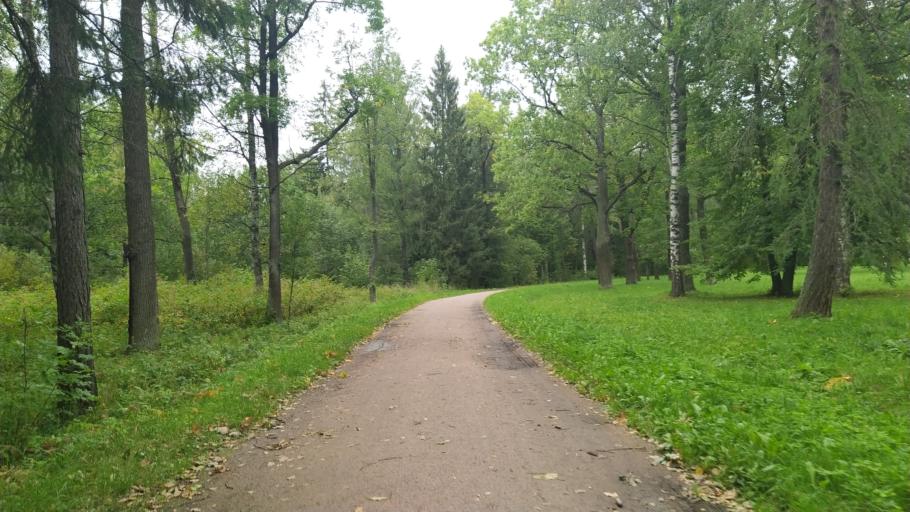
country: RU
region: St.-Petersburg
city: Pushkin
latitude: 59.7183
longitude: 30.3821
